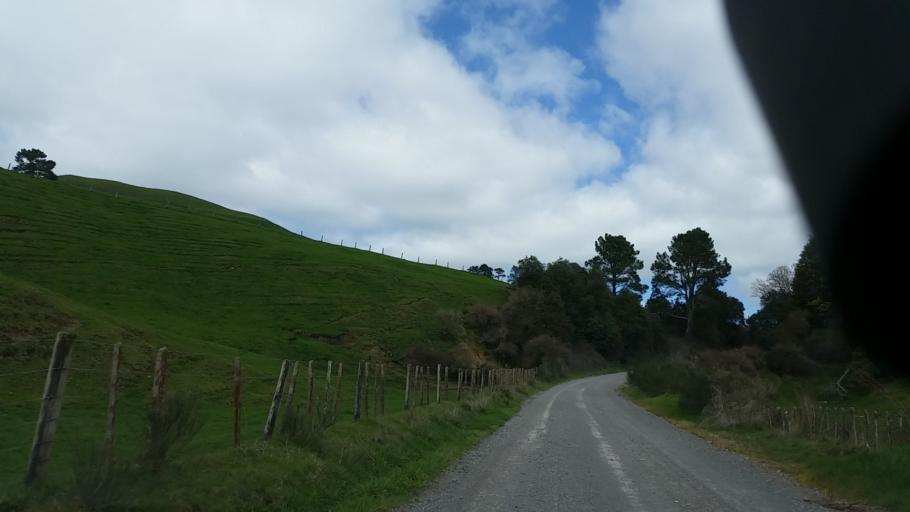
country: NZ
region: Bay of Plenty
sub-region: Rotorua District
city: Rotorua
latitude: -38.3824
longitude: 176.2014
